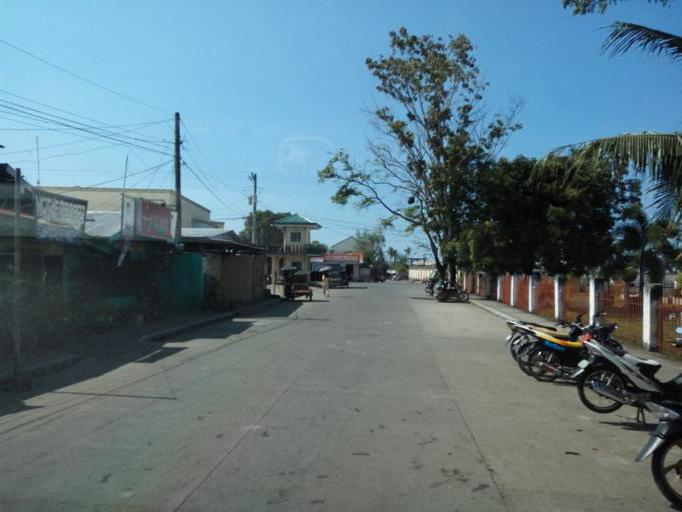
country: PH
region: Cagayan Valley
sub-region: Province of Cagayan
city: Gonzaga
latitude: 18.2607
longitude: 121.9965
